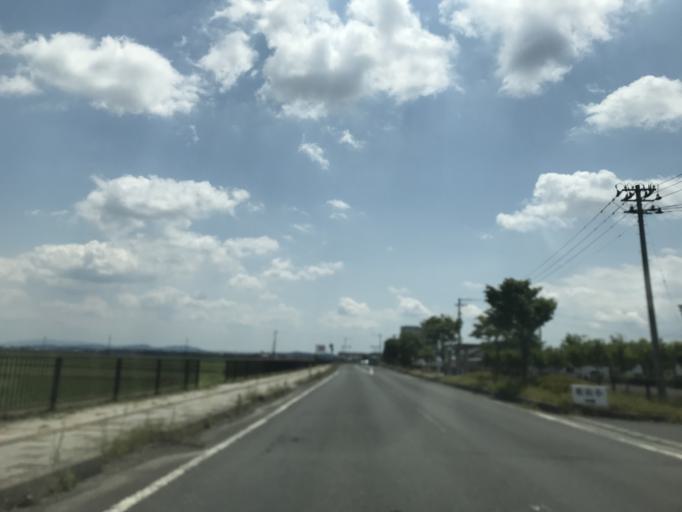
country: JP
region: Miyagi
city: Kogota
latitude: 38.5171
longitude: 141.0586
